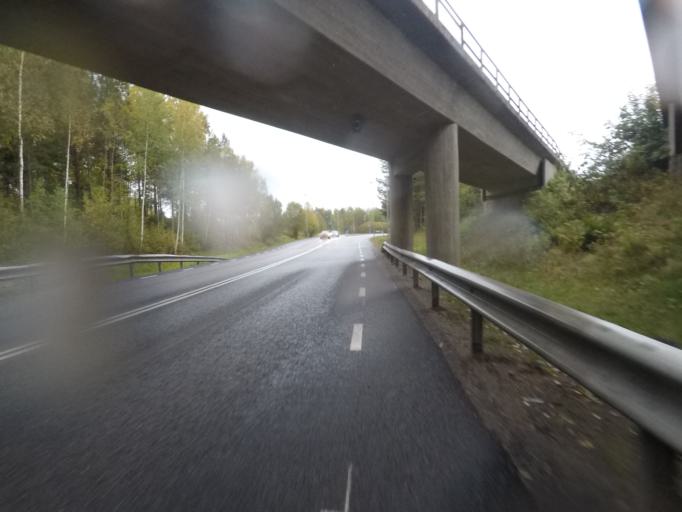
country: SE
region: OErebro
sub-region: Karlskoga Kommun
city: Karlskoga
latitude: 59.3174
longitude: 14.4723
